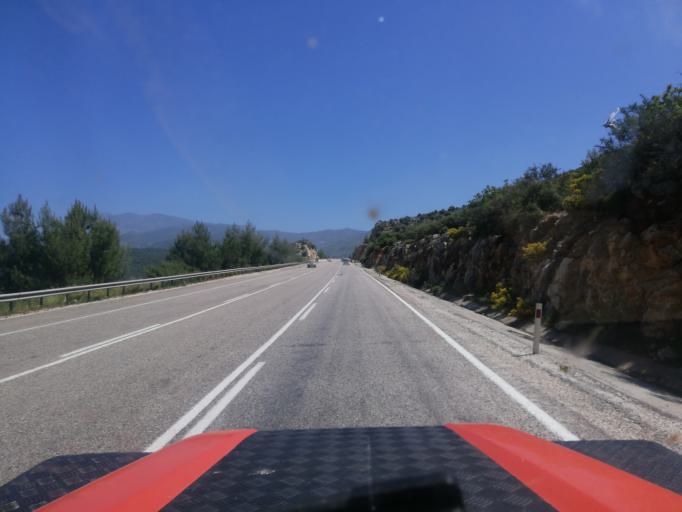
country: TR
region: Antalya
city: Kalkan
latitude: 36.2755
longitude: 29.3809
